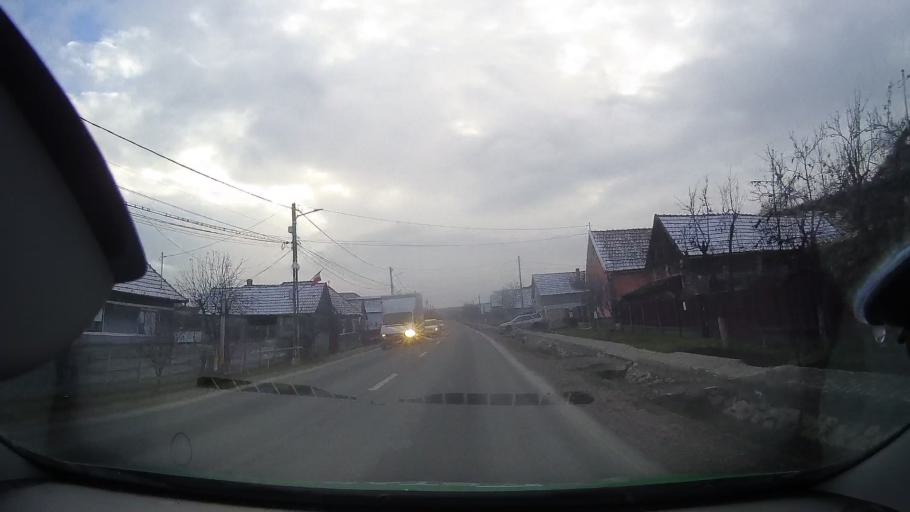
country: RO
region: Mures
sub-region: Comuna Cucerdea
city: Cucerdea
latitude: 46.3976
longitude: 24.2600
